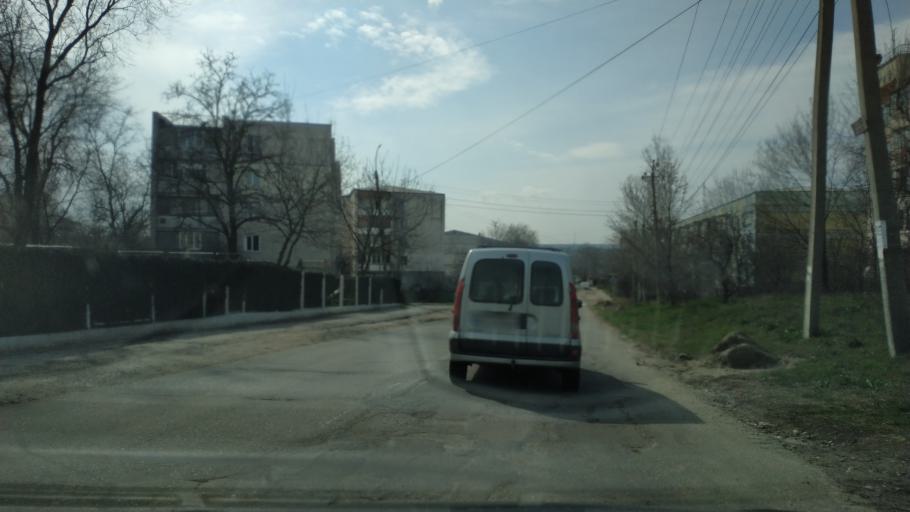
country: MD
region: Gagauzia
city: Vulcanesti
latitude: 45.6884
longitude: 28.4067
